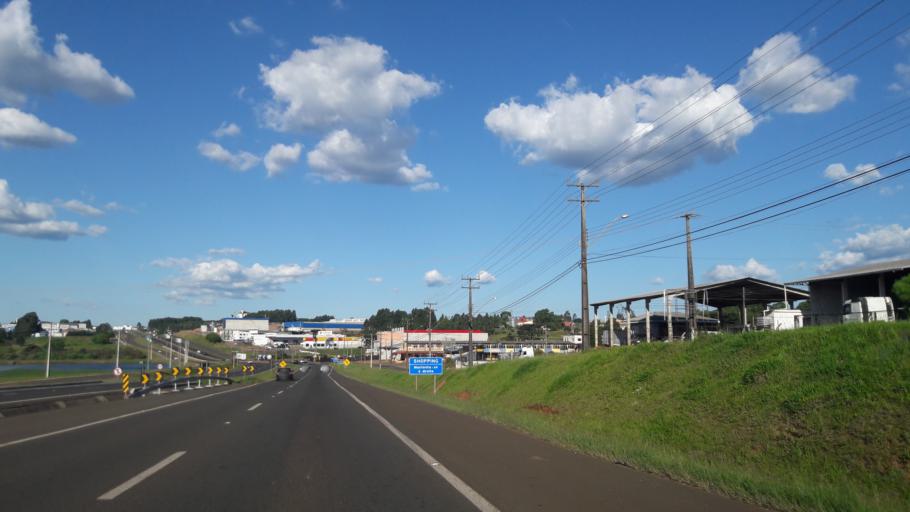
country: BR
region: Parana
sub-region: Guarapuava
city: Guarapuava
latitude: -25.3591
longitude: -51.4660
